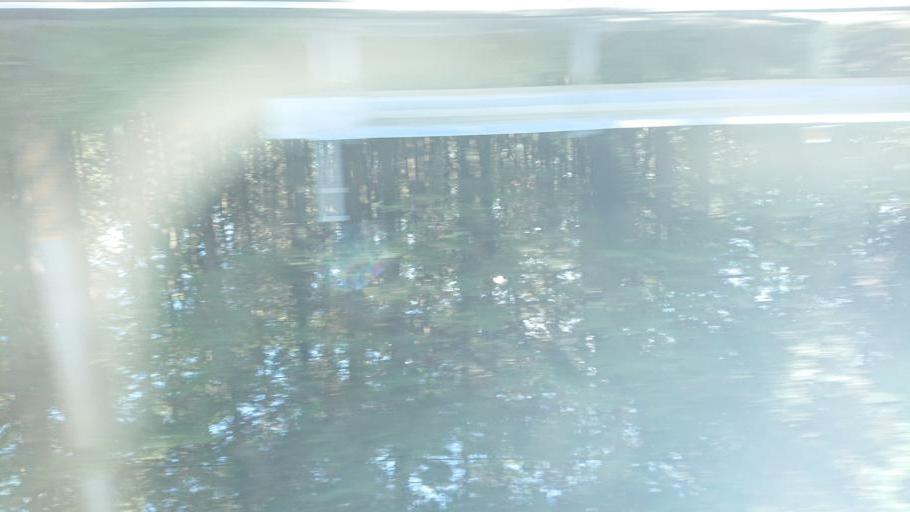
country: TW
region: Taiwan
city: Lugu
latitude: 23.4952
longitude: 120.8203
